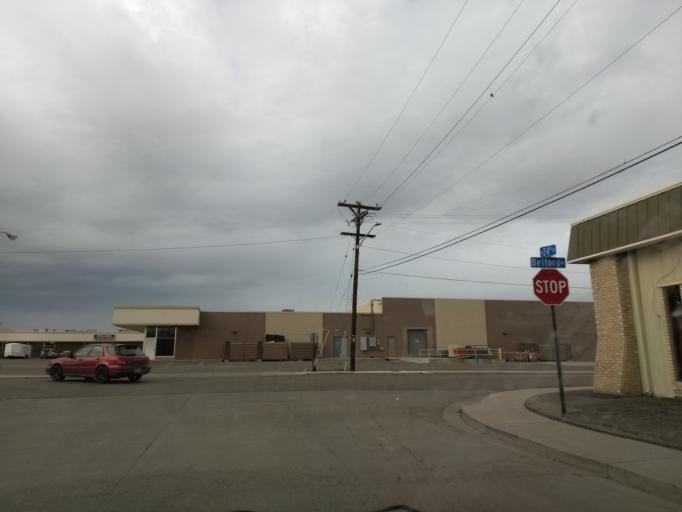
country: US
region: Colorado
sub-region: Mesa County
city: Grand Junction
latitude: 39.0753
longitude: -108.5374
